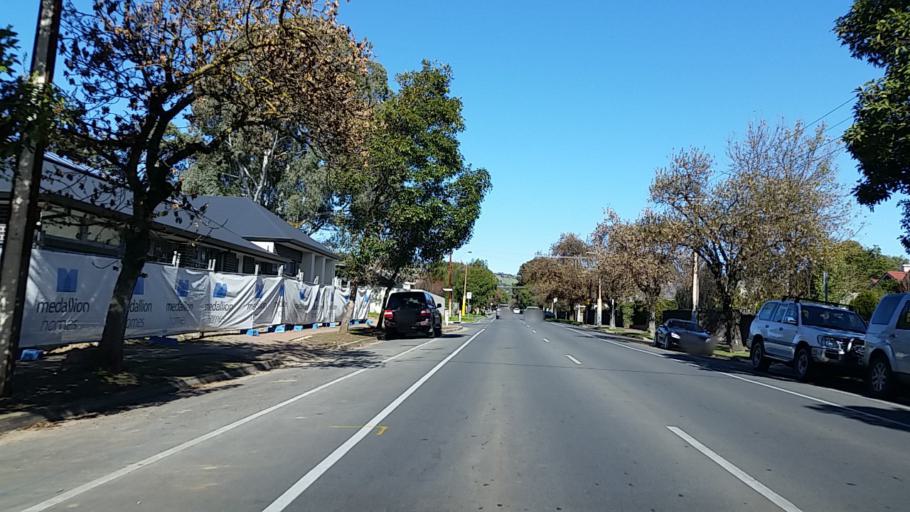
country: AU
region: South Australia
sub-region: Burnside
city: Leabrook
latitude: -34.9284
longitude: 138.6512
